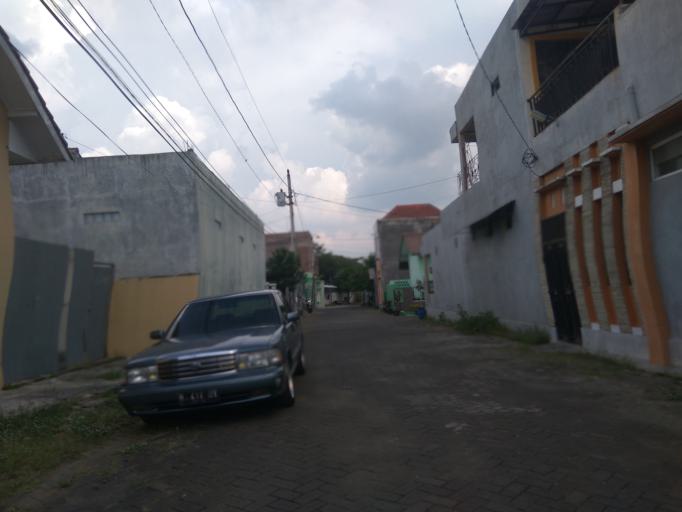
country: ID
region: Central Java
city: Semarang
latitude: -7.0647
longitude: 110.4460
